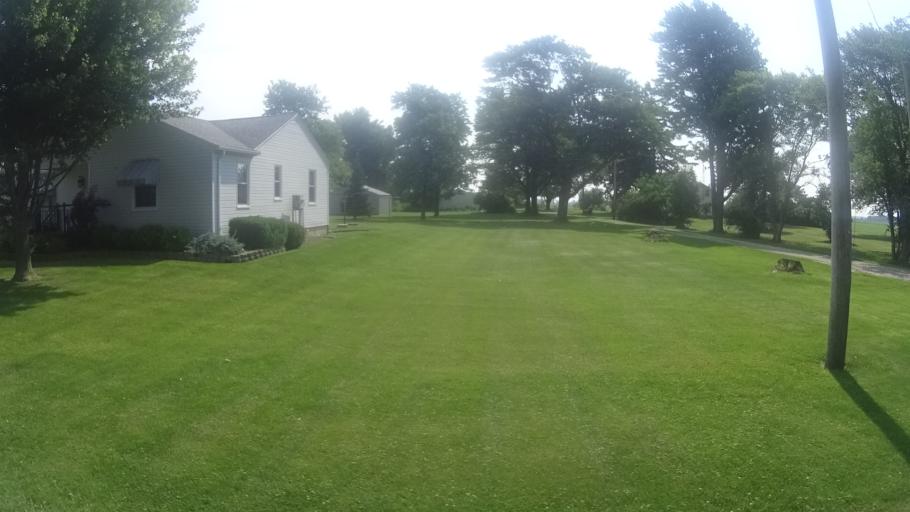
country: US
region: Ohio
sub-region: Huron County
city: Monroeville
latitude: 41.3266
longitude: -82.7188
